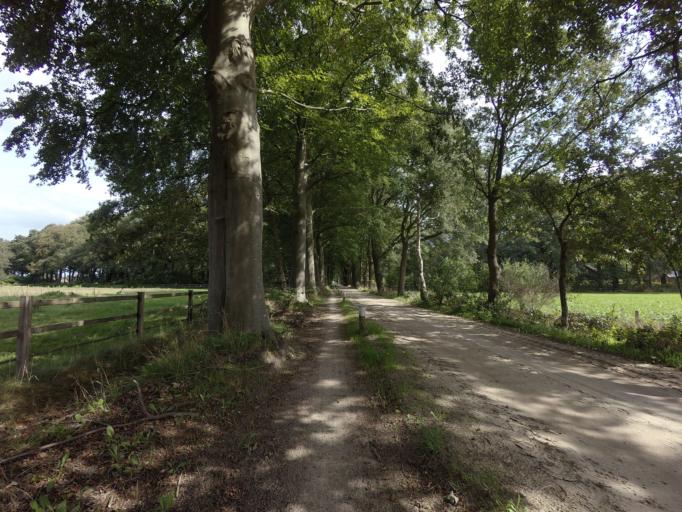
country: NL
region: Overijssel
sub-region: Gemeente Deventer
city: Schalkhaar
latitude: 52.2877
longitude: 6.2455
